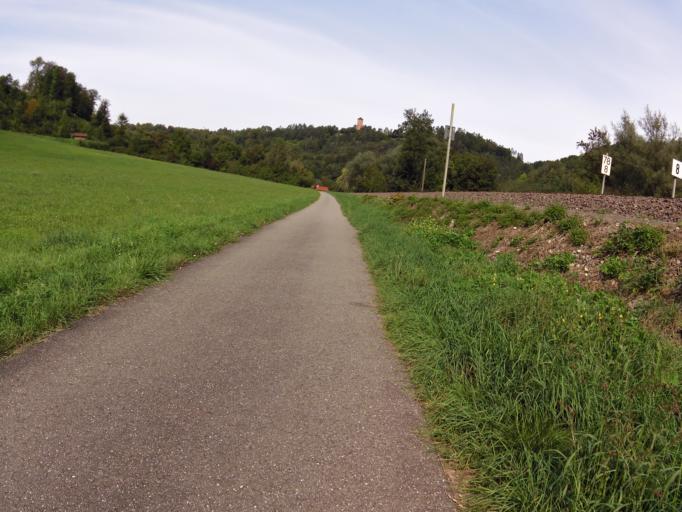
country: DE
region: Baden-Wuerttemberg
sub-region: Karlsruhe Region
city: Horb am Neckar
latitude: 48.4451
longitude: 8.7067
